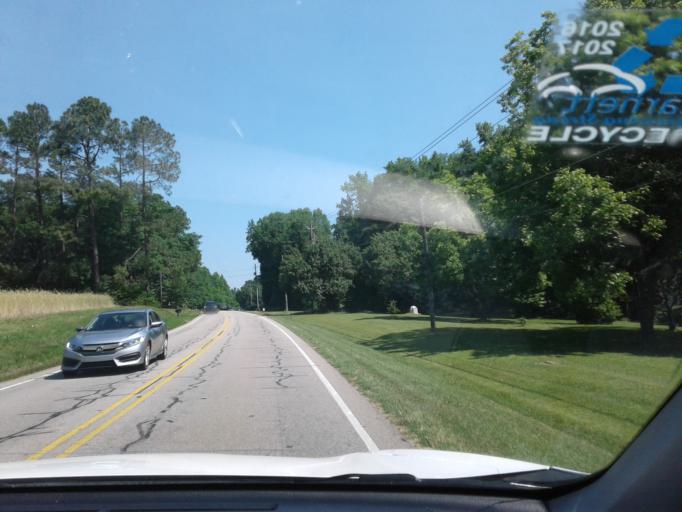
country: US
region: North Carolina
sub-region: Wake County
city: Holly Springs
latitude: 35.6112
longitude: -78.8403
